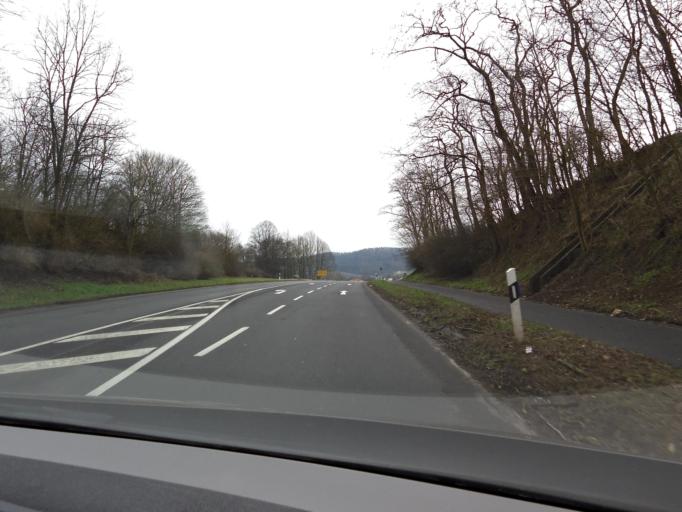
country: DE
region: Hesse
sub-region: Regierungsbezirk Kassel
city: Eschwege
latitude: 51.1765
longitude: 10.0767
